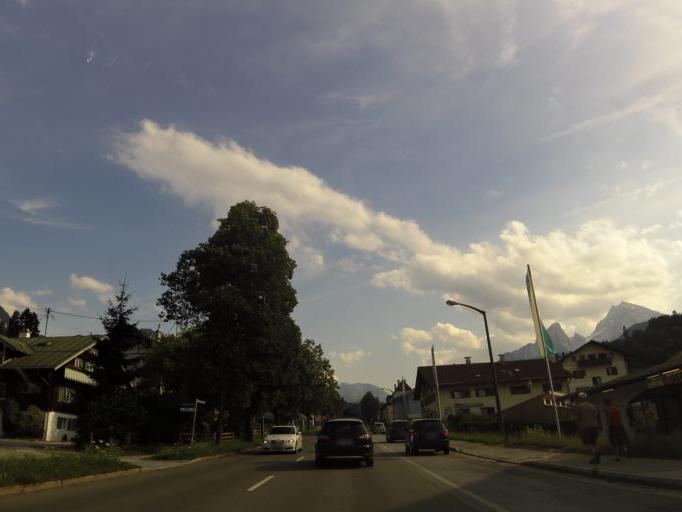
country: DE
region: Bavaria
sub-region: Upper Bavaria
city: Berchtesgaden
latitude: 47.6229
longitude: 13.0010
